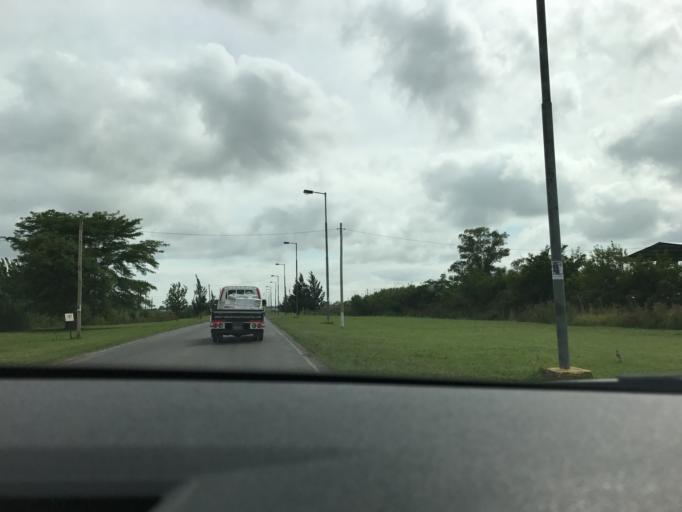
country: AR
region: Buenos Aires
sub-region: Partido de La Plata
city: La Plata
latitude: -34.8443
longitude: -58.0752
